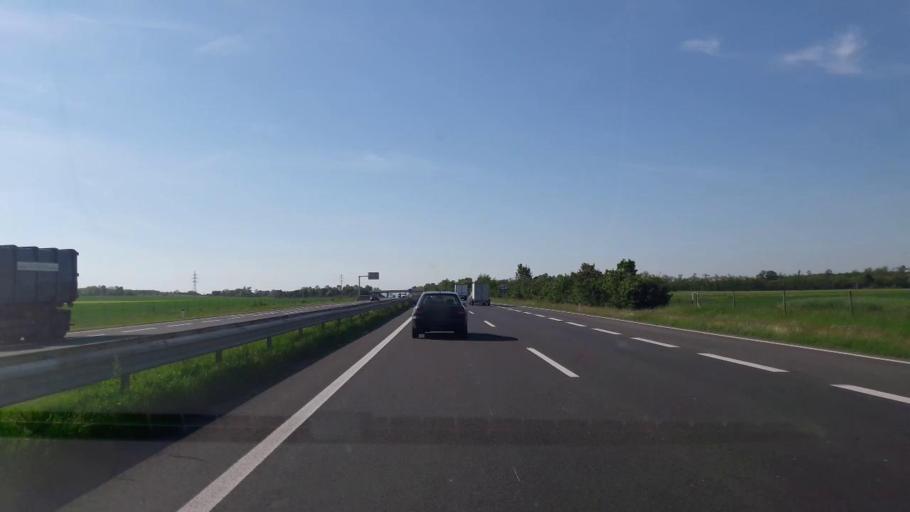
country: AT
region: Burgenland
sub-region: Eisenstadt-Umgebung
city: Hornstein
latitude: 47.8643
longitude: 16.4205
